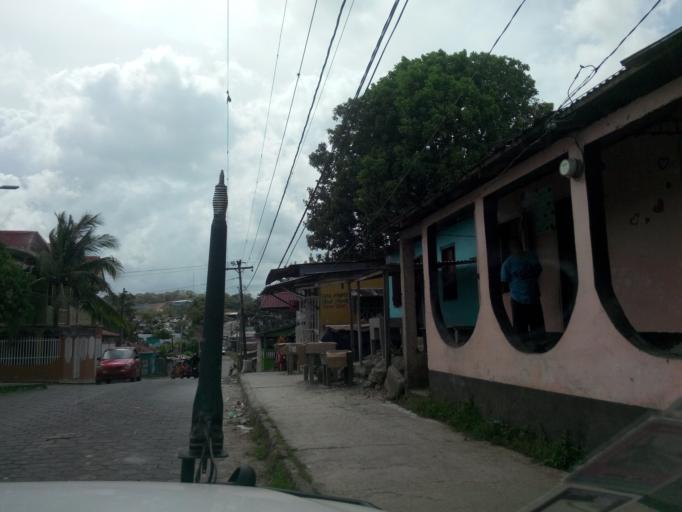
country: NI
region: Atlantico Sur
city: Bluefields
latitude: 12.0118
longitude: -83.7682
